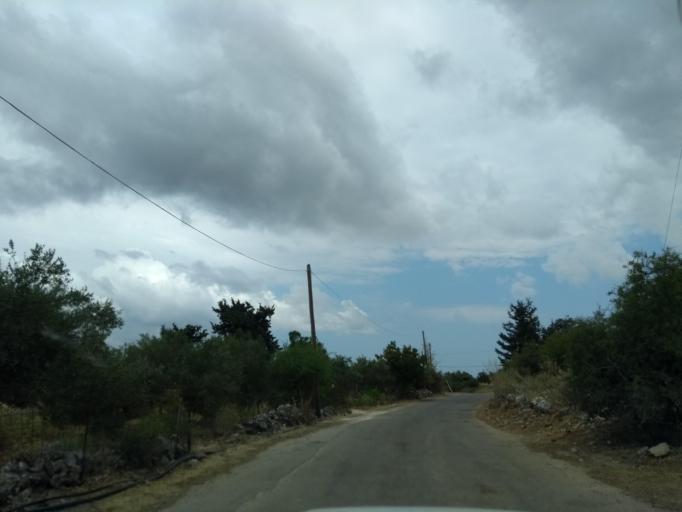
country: GR
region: Crete
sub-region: Nomos Chanias
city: Georgioupolis
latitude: 35.4022
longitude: 24.2240
